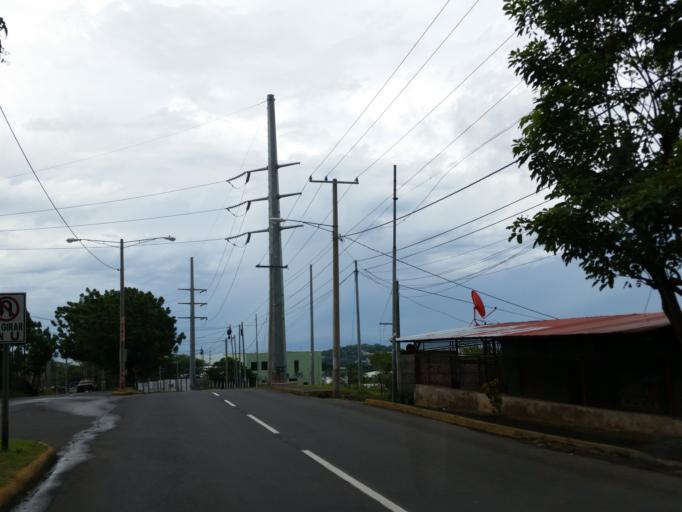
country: NI
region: Managua
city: Managua
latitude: 12.1196
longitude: -86.2834
